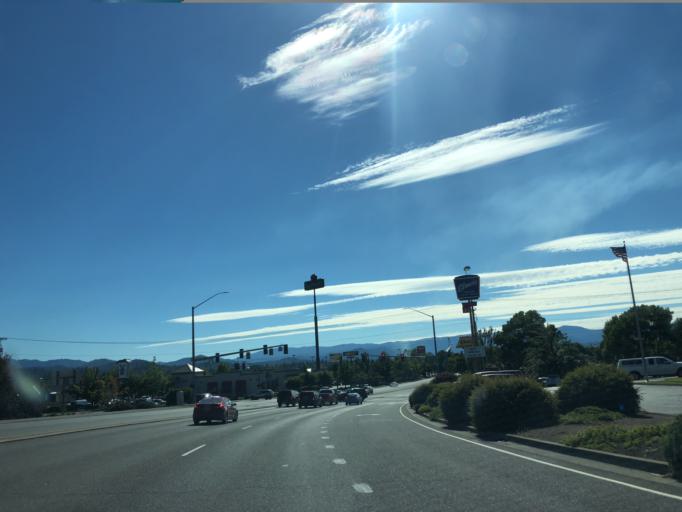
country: US
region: Oregon
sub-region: Josephine County
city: Fruitdale
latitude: 42.4368
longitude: -123.2967
